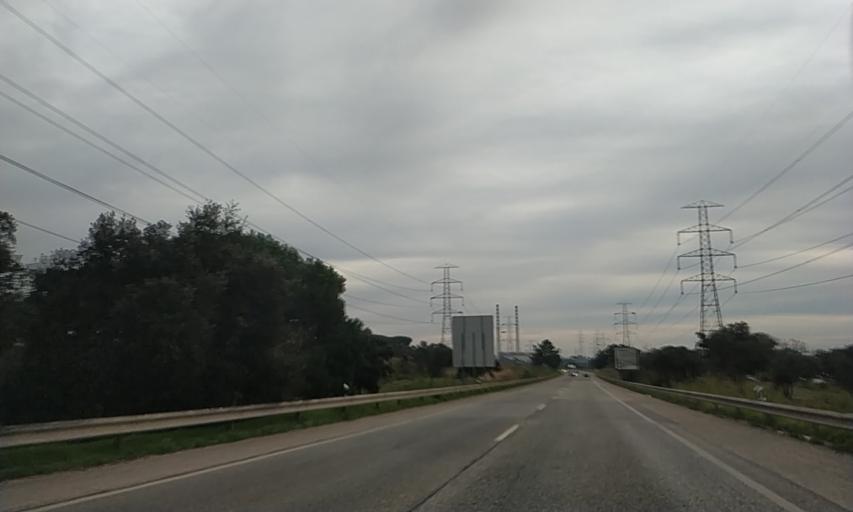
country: PT
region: Setubal
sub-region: Setubal
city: Setubal
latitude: 38.5311
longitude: -8.8431
